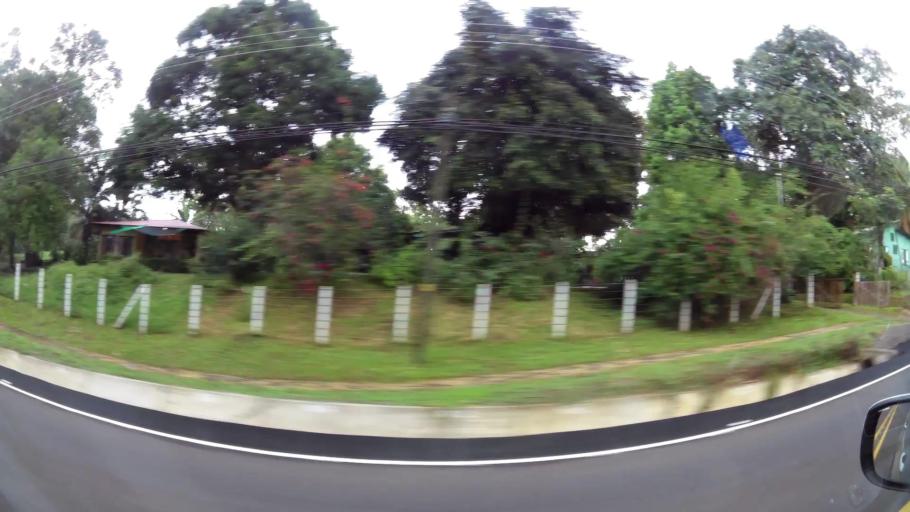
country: CR
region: Alajuela
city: Desamparados
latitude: 9.9434
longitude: -84.5418
